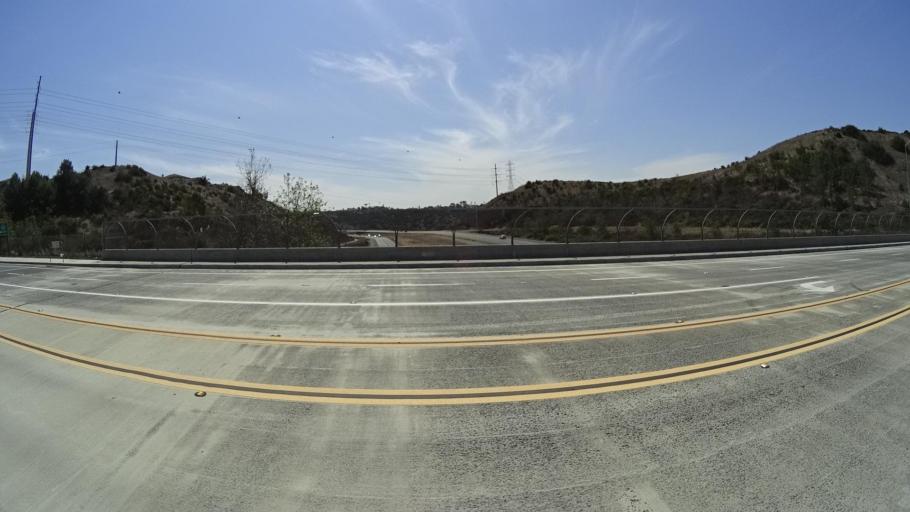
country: US
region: California
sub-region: San Diego County
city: La Presa
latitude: 32.6709
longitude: -116.9847
